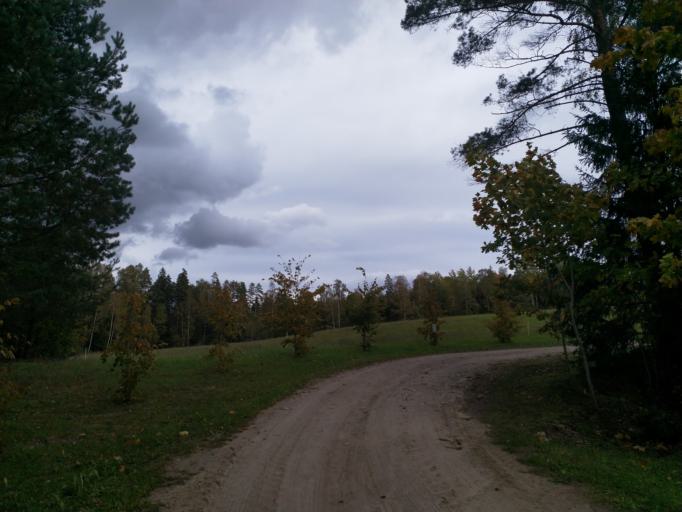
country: LV
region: Alsunga
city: Alsunga
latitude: 57.0419
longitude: 21.6911
